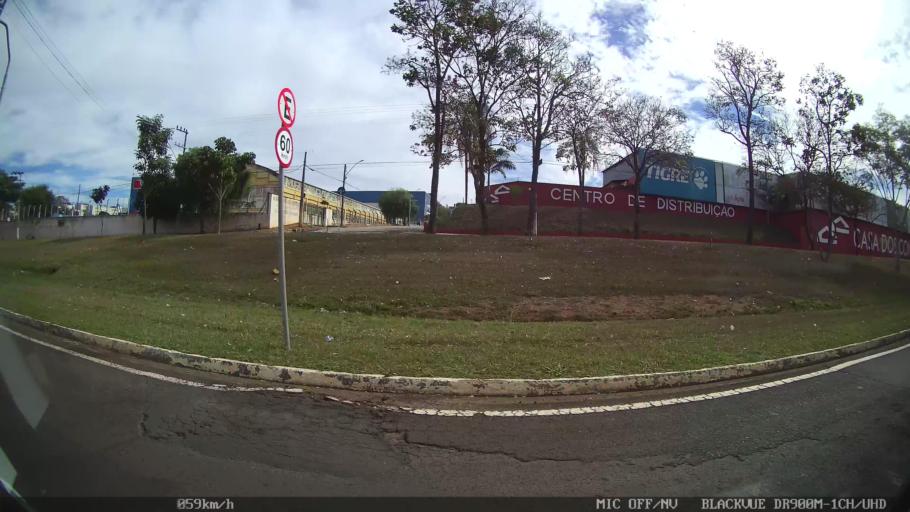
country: BR
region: Sao Paulo
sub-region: Catanduva
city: Catanduva
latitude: -21.1552
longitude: -48.9834
